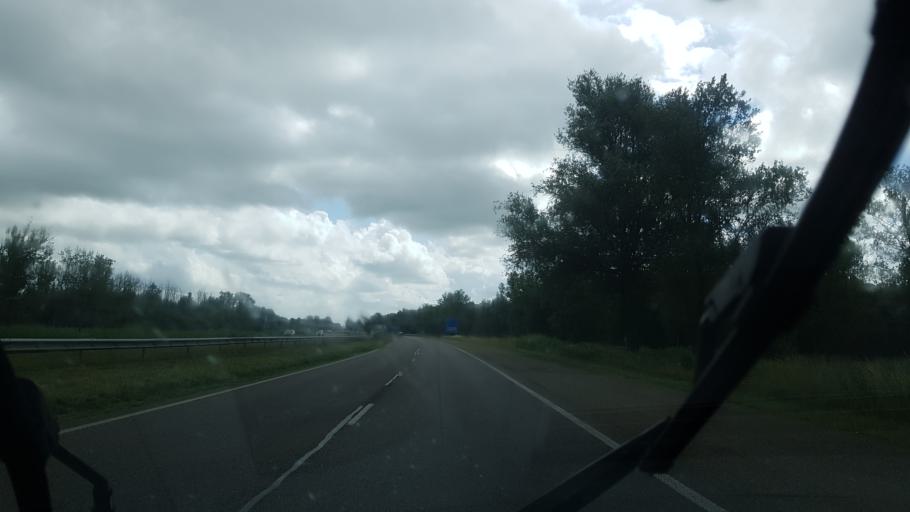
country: NL
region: Friesland
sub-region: Gemeente Leeuwarden
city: Camminghaburen
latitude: 53.2168
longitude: 5.8554
